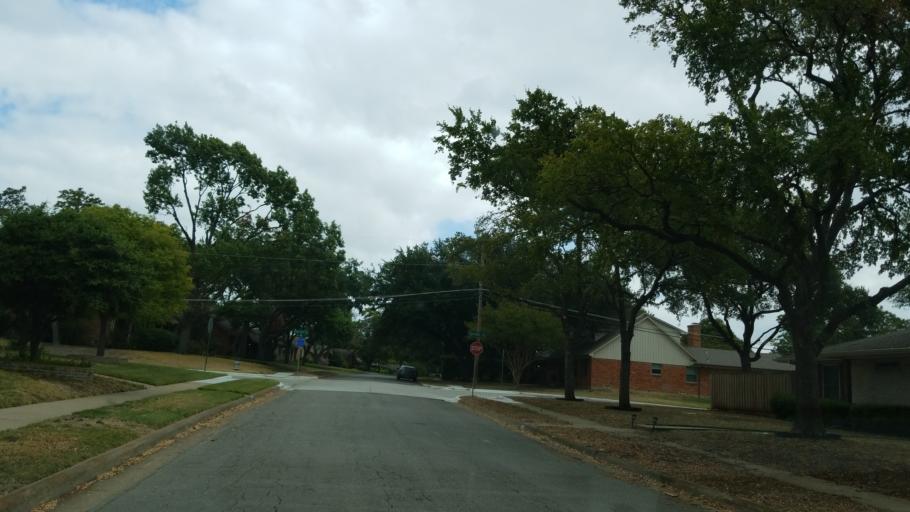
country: US
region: Texas
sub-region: Dallas County
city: Richardson
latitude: 32.9356
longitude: -96.7733
